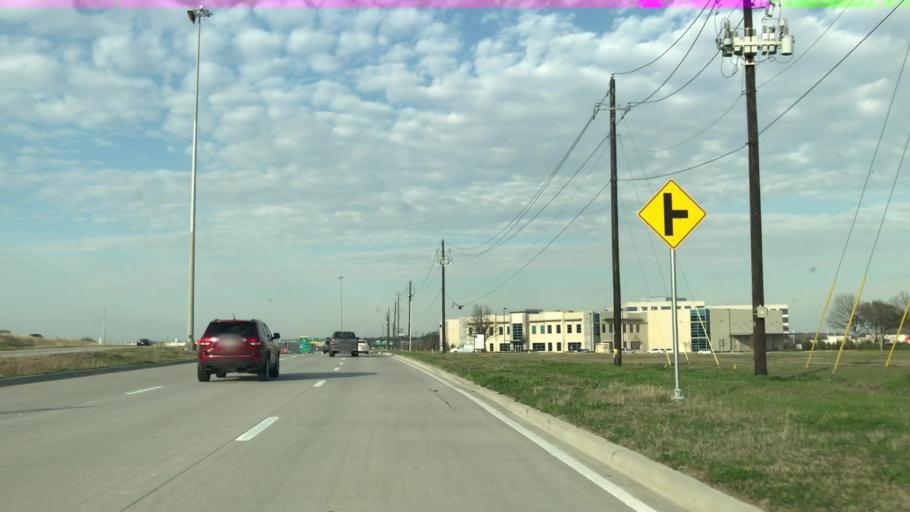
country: US
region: Texas
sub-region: Dallas County
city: Coppell
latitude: 32.9813
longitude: -97.0185
